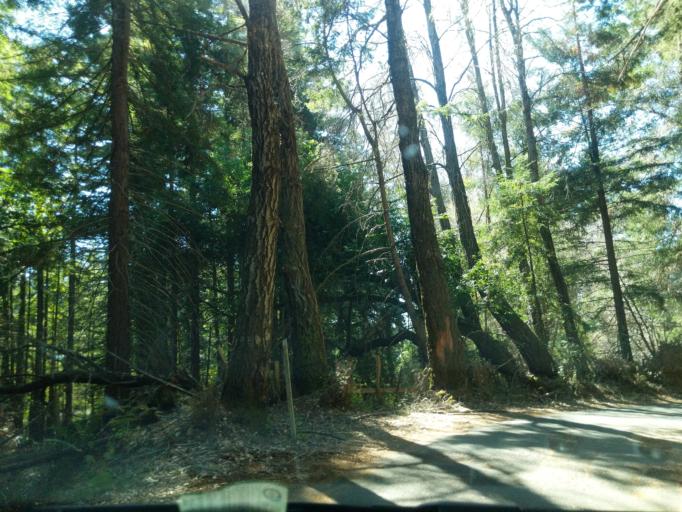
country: US
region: California
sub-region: Sonoma County
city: Monte Rio
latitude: 38.5236
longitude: -123.2308
